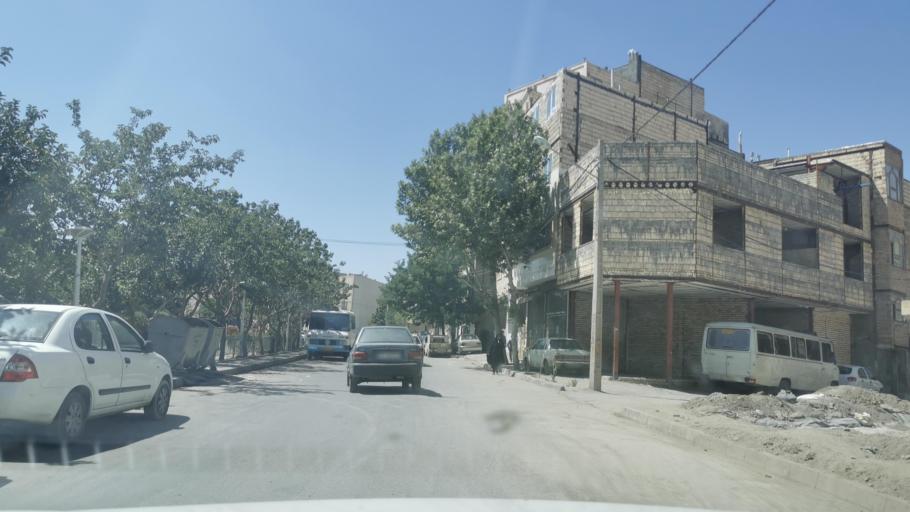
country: IR
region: Razavi Khorasan
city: Mashhad
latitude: 36.3613
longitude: 59.5553
